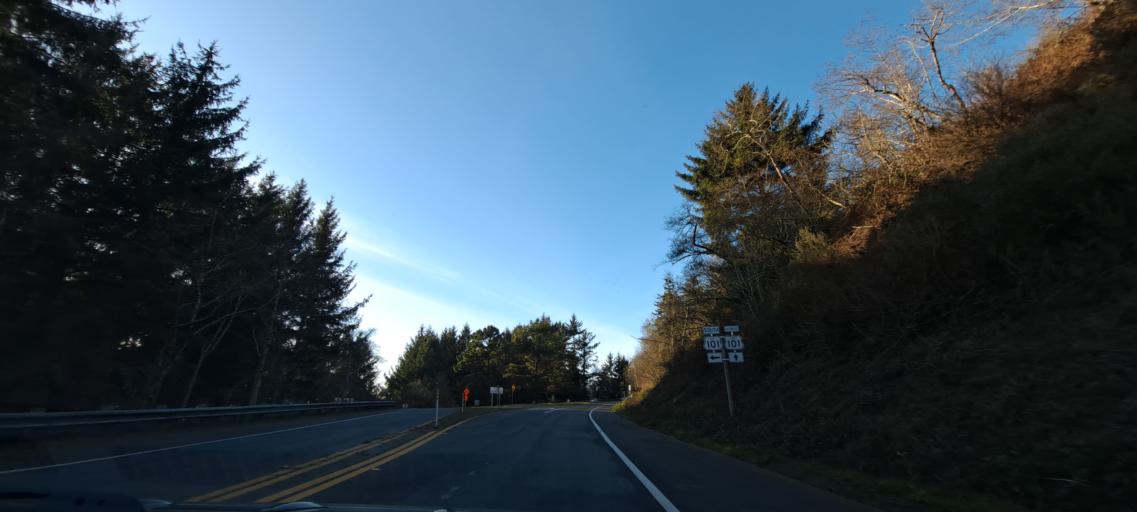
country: US
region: California
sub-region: Humboldt County
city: McKinleyville
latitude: 40.9223
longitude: -124.0979
